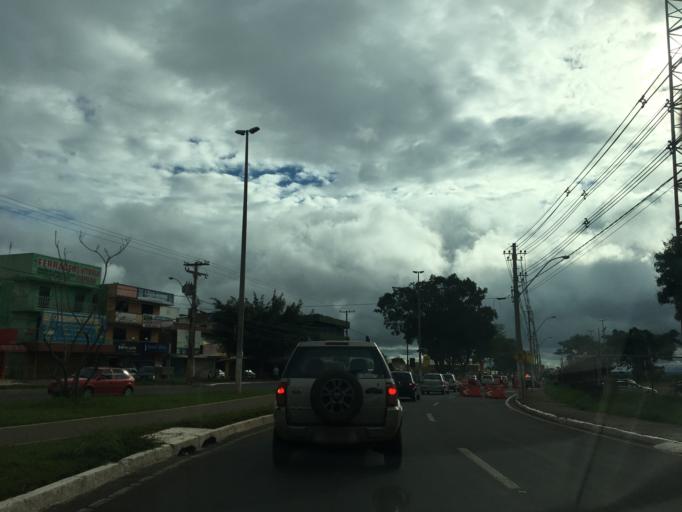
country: BR
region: Goias
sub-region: Luziania
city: Luziania
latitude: -16.0169
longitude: -48.0178
